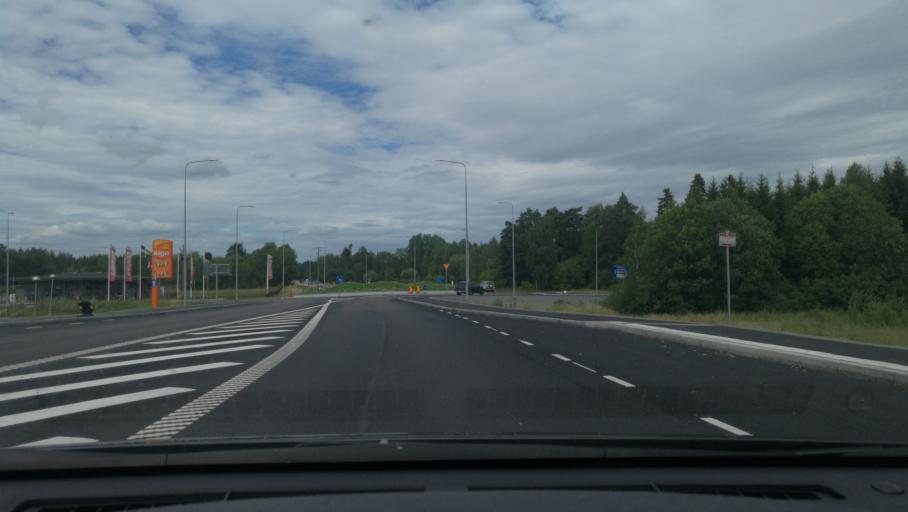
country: SE
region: Uppsala
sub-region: Enkopings Kommun
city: Enkoping
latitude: 59.6574
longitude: 17.0787
